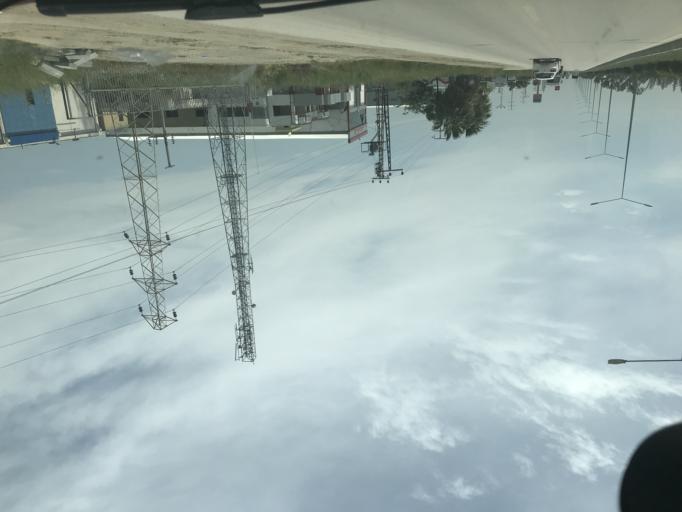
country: TR
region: Adana
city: Yuregir
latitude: 36.9824
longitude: 35.4247
